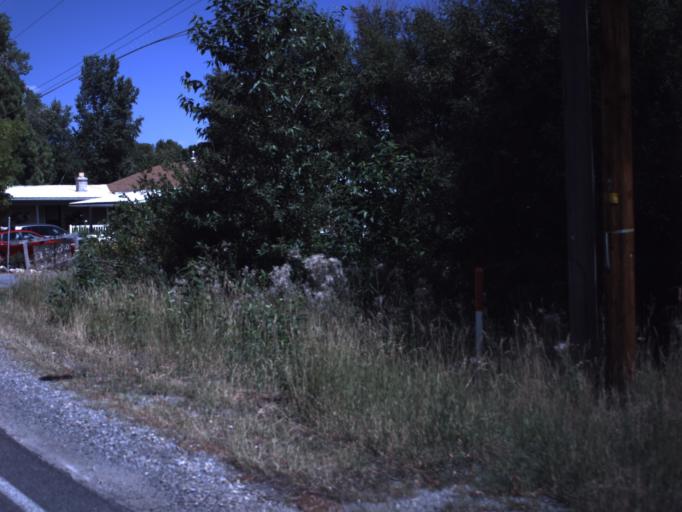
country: US
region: Idaho
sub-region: Bear Lake County
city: Paris
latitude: 41.9251
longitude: -111.3971
